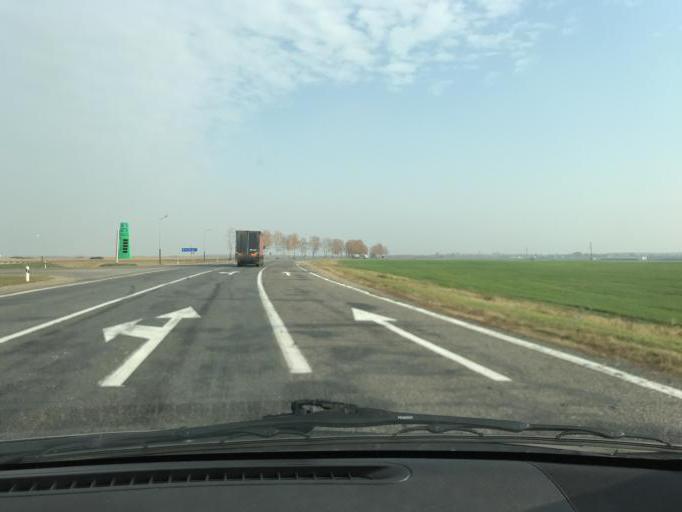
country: BY
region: Vitebsk
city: Chashniki
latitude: 55.0159
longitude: 29.1733
